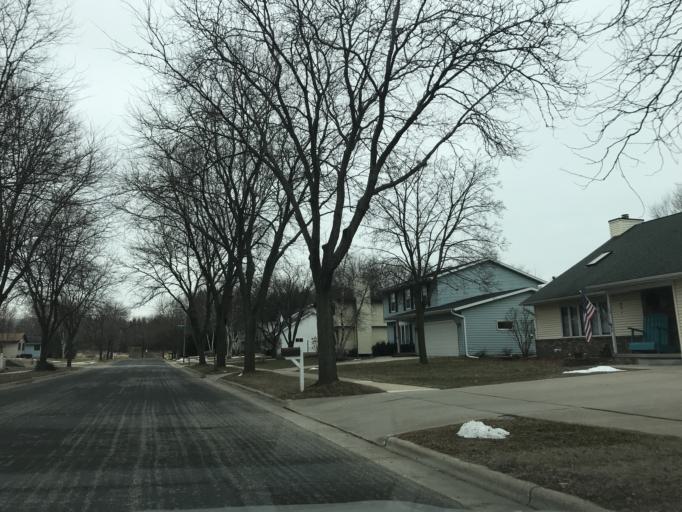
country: US
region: Wisconsin
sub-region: Dane County
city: Monona
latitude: 43.0980
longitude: -89.2958
